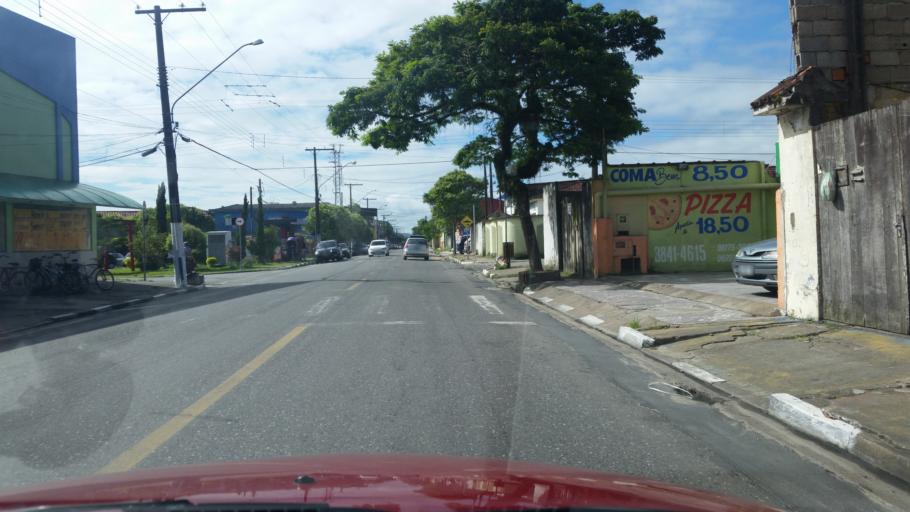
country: BR
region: Sao Paulo
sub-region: Iguape
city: Iguape
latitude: -24.7006
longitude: -47.5622
